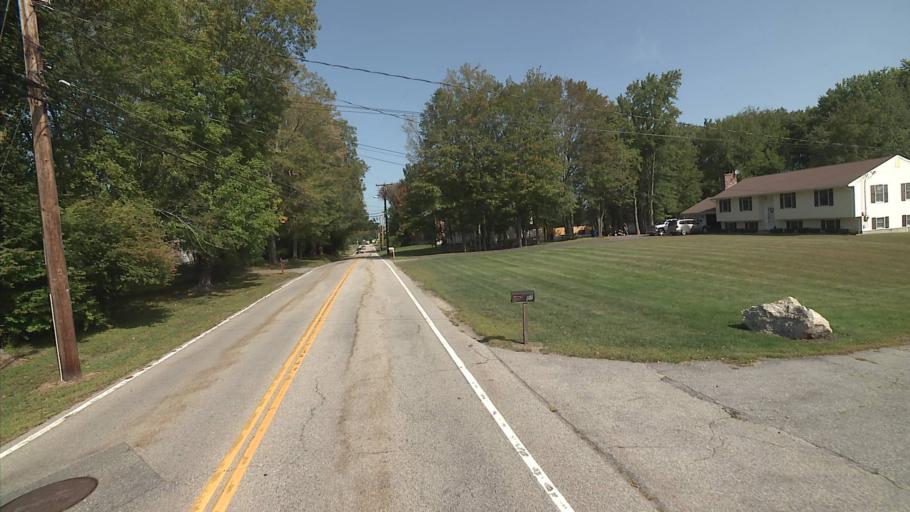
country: US
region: Connecticut
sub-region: Windham County
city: South Woodstock
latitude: 41.9314
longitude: -71.9569
